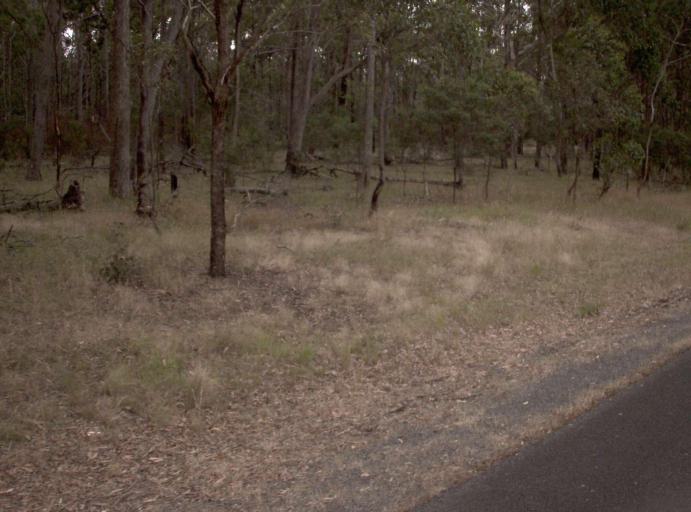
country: AU
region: Victoria
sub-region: Wellington
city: Sale
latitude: -38.4442
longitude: 146.9443
